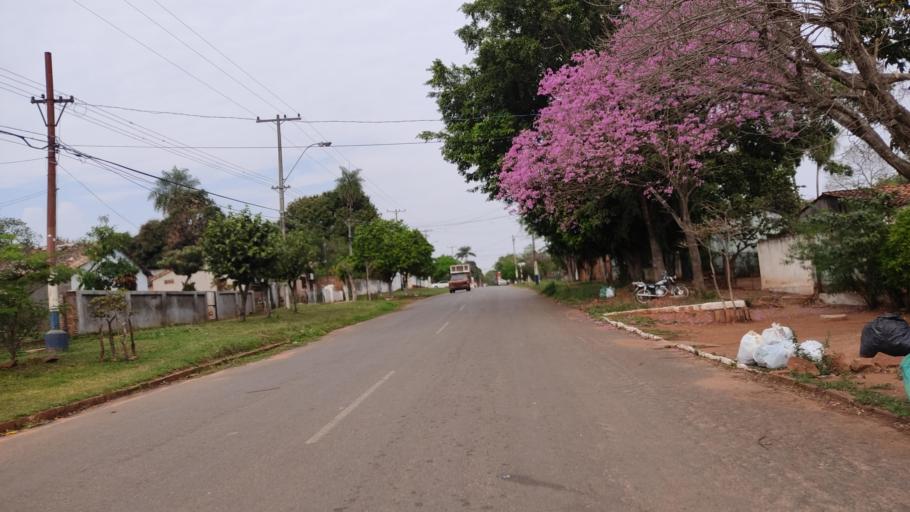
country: PY
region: Misiones
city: San Juan Bautista
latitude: -26.6634
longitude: -57.1500
